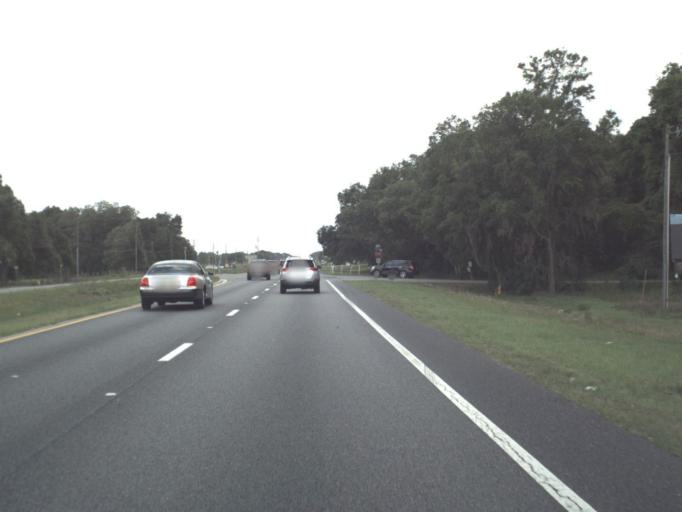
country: US
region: Florida
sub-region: Marion County
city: Belleview
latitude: 29.0267
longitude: -82.0202
